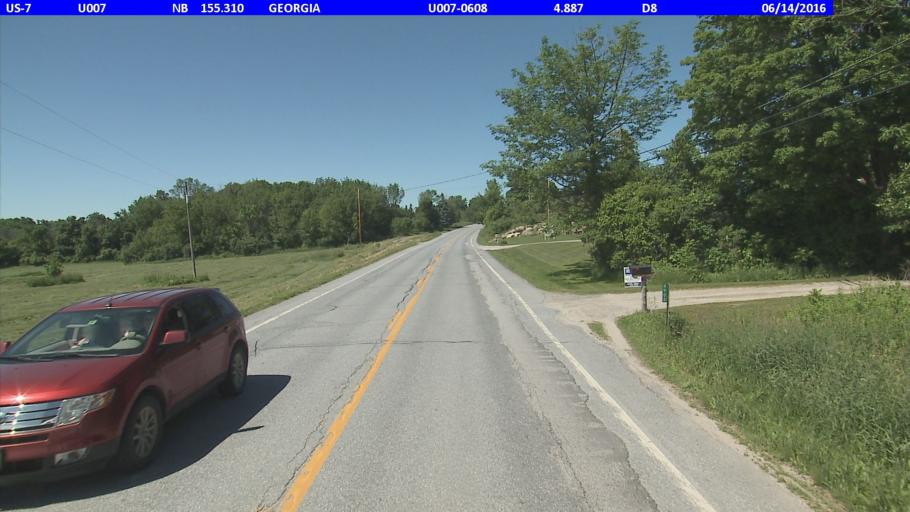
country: US
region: Vermont
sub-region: Franklin County
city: Saint Albans
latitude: 44.7416
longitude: -73.1145
